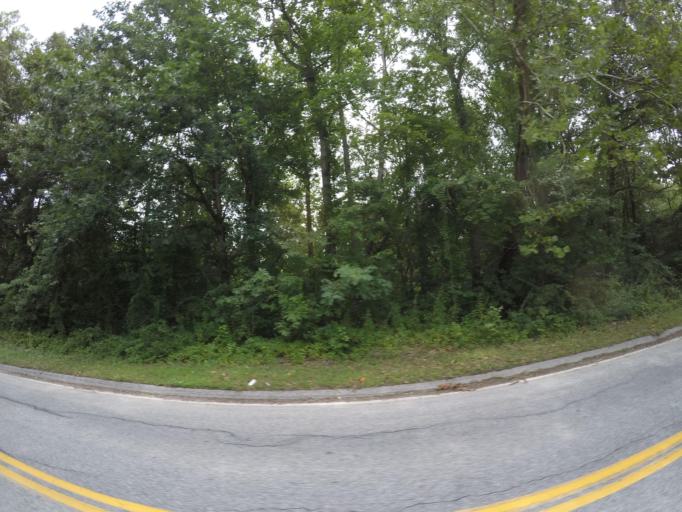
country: US
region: Maryland
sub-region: Anne Arundel County
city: Crofton
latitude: 39.0339
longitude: -76.7139
